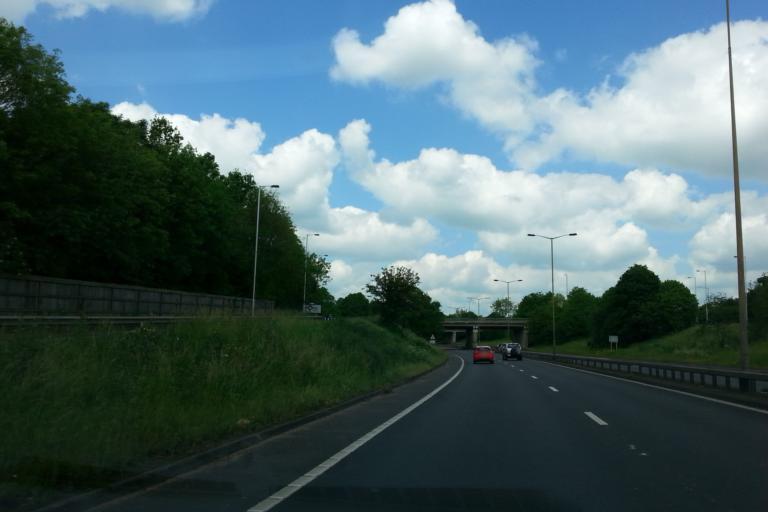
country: GB
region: England
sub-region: Peterborough
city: Peterborough
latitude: 52.5498
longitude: -0.2660
